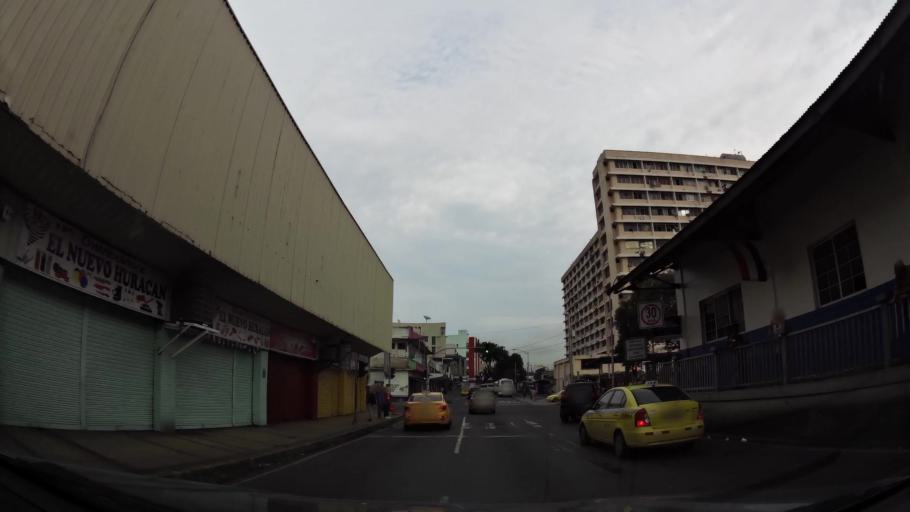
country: PA
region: Panama
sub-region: Distrito de Panama
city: Ancon
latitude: 8.9578
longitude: -79.5392
